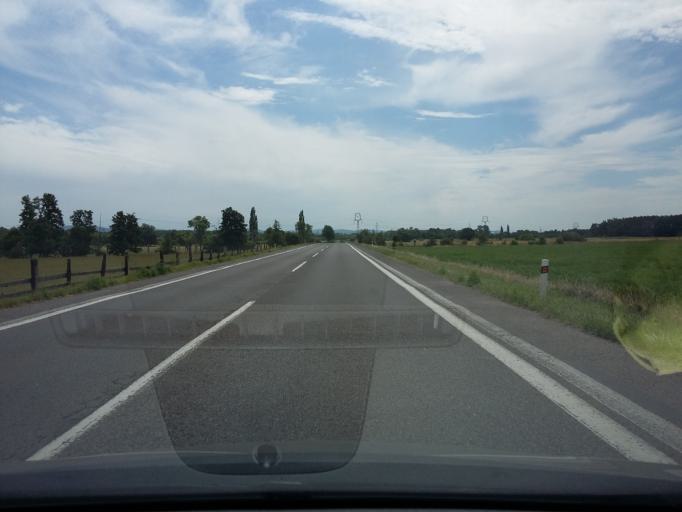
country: SK
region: Bratislavsky
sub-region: Okres Malacky
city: Malacky
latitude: 48.4905
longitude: 17.0089
